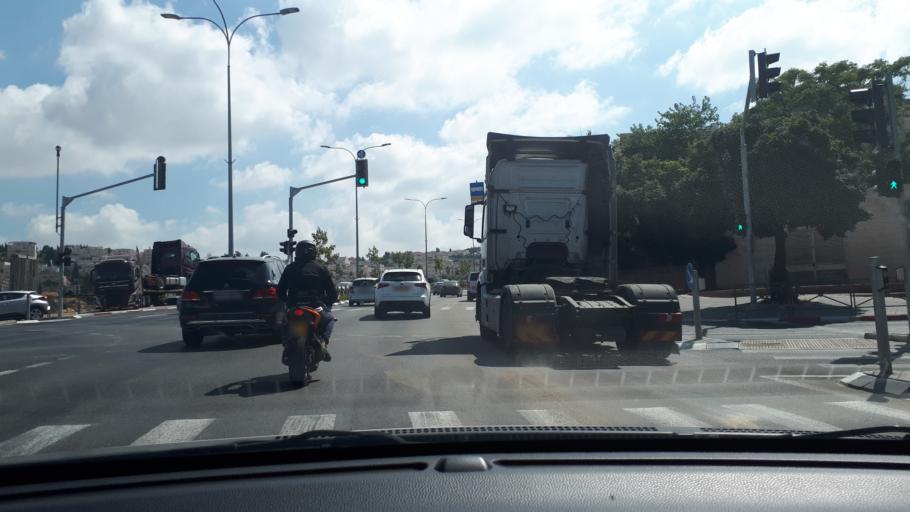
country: PS
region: West Bank
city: Hizma
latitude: 31.8274
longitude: 35.2454
